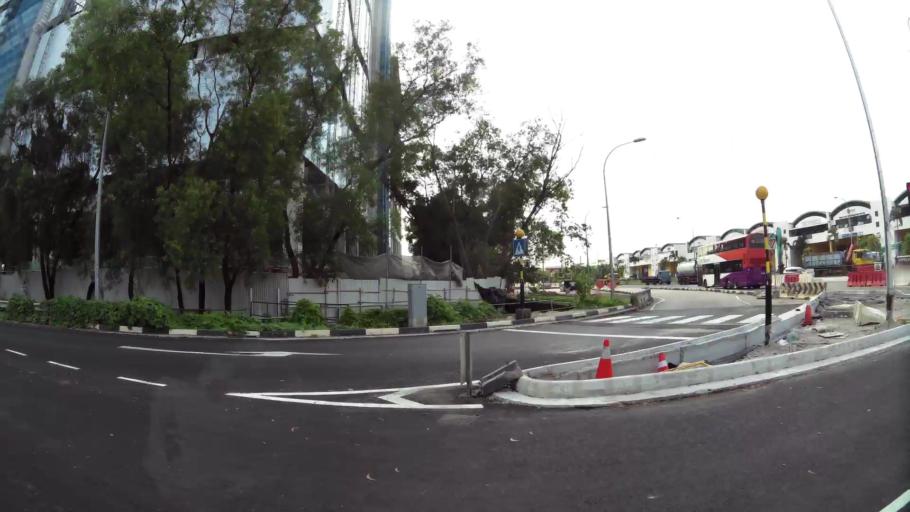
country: MY
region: Johor
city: Johor Bahru
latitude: 1.3146
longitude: 103.6562
